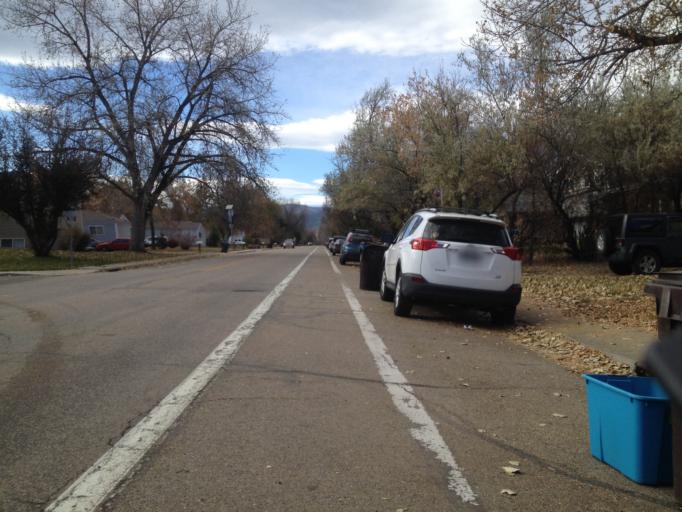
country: US
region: Colorado
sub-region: Boulder County
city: Boulder
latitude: 39.9950
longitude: -105.2512
